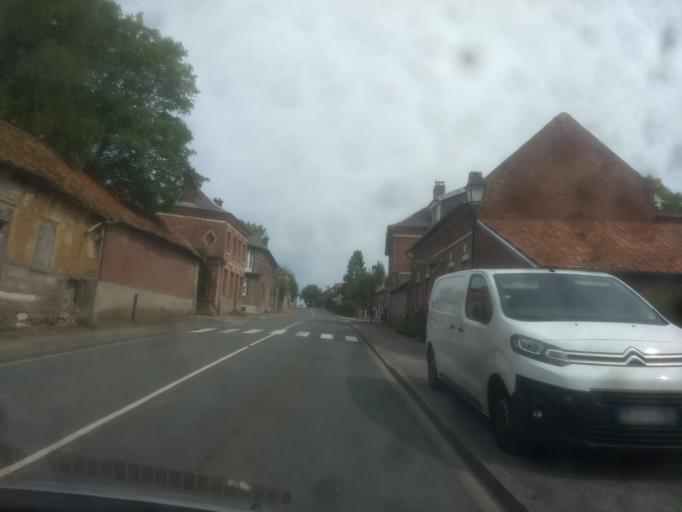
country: FR
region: Picardie
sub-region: Departement de la Somme
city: Saint-Riquier
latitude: 50.1367
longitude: 1.9460
